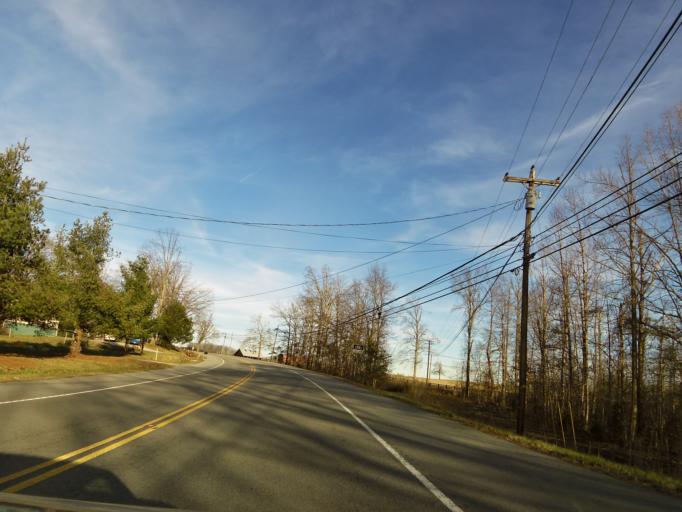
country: US
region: Tennessee
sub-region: White County
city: Sparta
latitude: 35.9386
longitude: -85.3456
